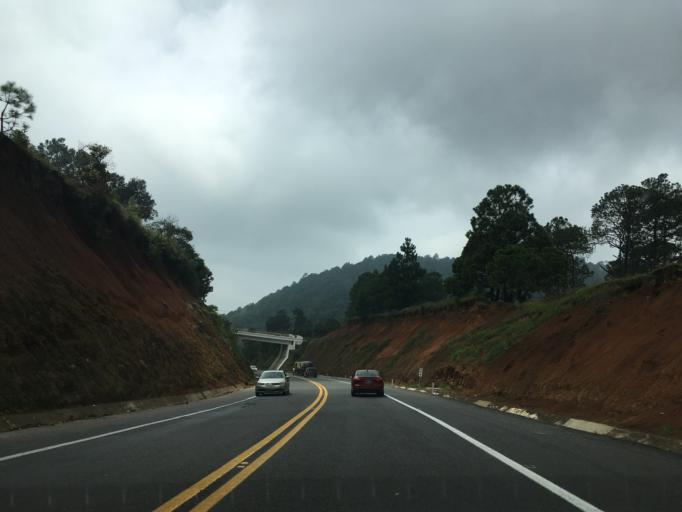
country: MX
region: Michoacan
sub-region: Ziracuaretiro
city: Patuan
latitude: 19.4402
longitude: -101.8864
